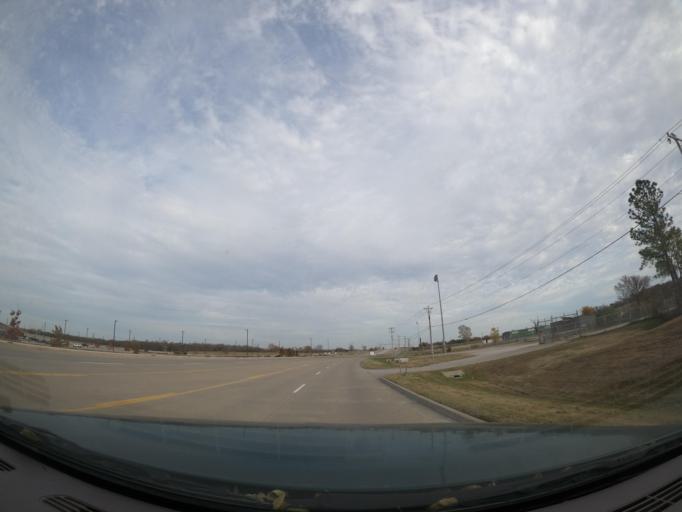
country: US
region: Oklahoma
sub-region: Tulsa County
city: Turley
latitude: 36.2057
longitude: -96.0039
